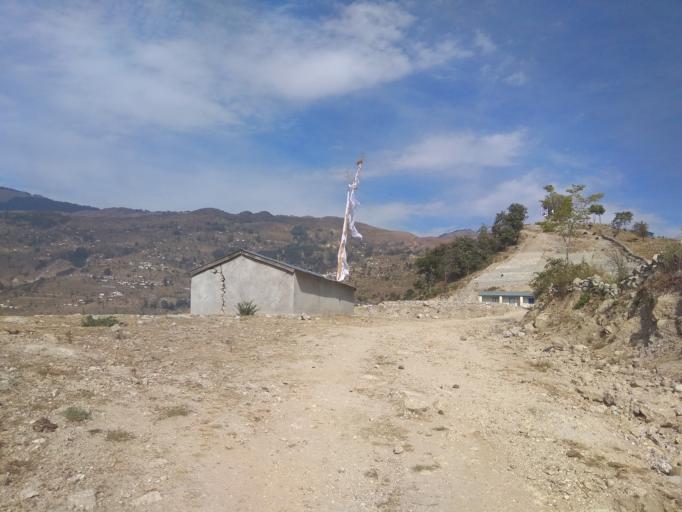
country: NP
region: Far Western
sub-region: Seti Zone
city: Achham
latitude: 29.2376
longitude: 81.6344
